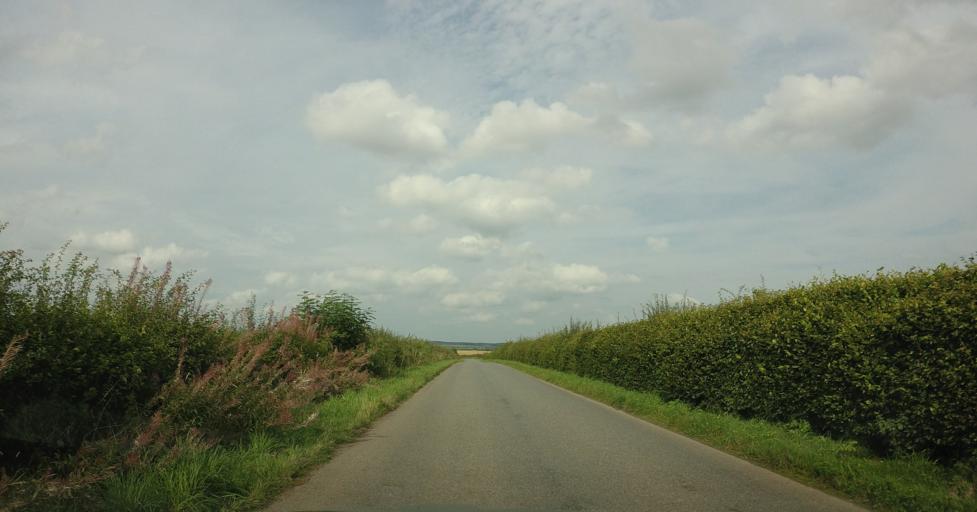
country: GB
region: Scotland
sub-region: Perth and Kinross
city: Auchterarder
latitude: 56.3650
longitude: -3.6968
